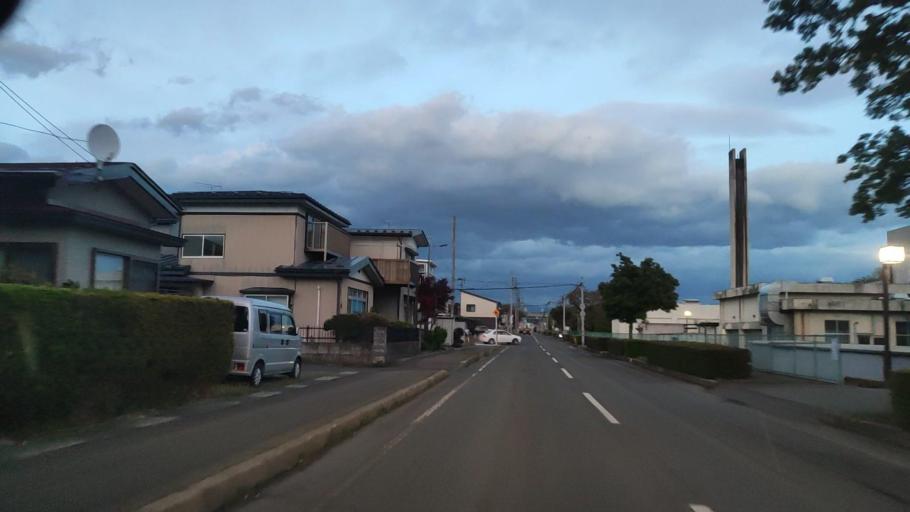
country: JP
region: Iwate
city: Morioka-shi
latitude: 39.7238
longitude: 141.1108
